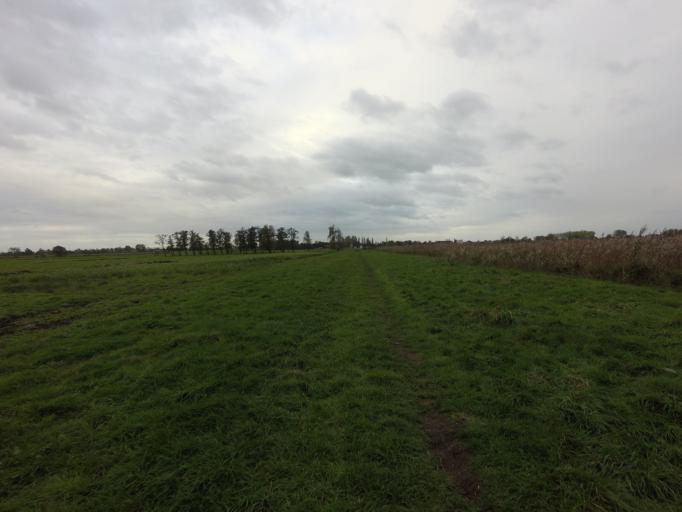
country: NL
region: Utrecht
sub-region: Gemeente De Ronde Venen
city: Mijdrecht
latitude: 52.2035
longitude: 4.9140
